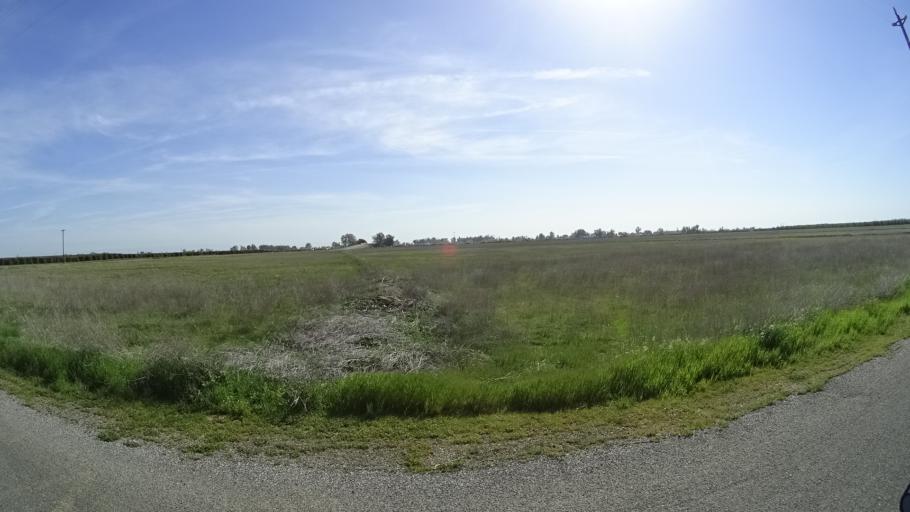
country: US
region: California
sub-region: Glenn County
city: Willows
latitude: 39.6236
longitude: -122.2130
